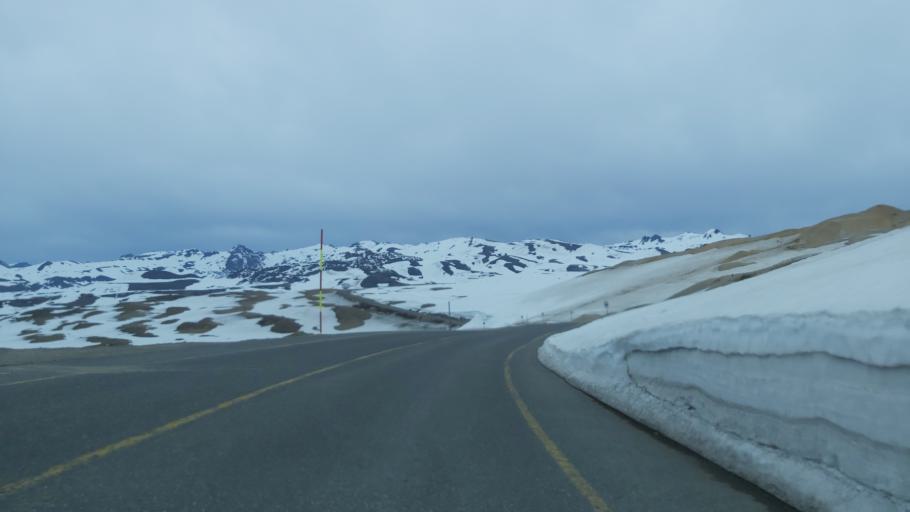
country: CL
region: Maule
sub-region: Provincia de Linares
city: Colbun
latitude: -36.0182
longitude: -70.5205
